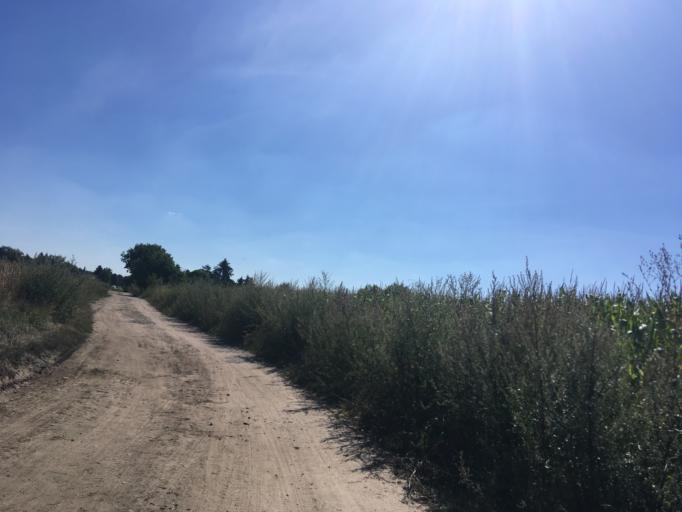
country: DE
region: Brandenburg
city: Altlandsberg
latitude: 52.5442
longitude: 13.7347
